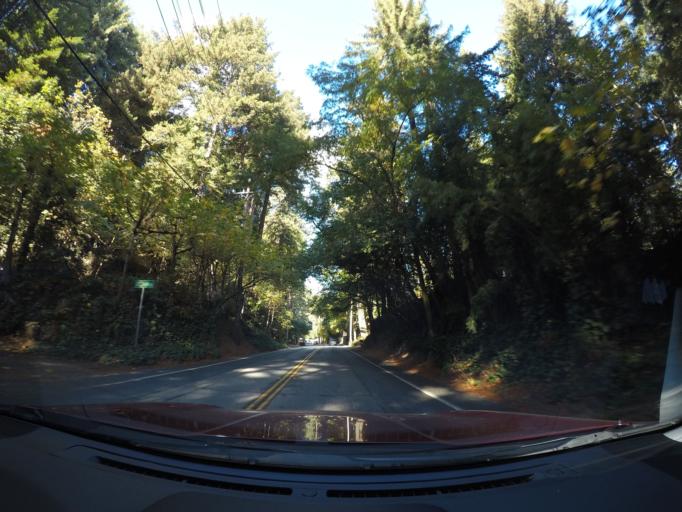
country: US
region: California
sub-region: Santa Cruz County
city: Ben Lomond
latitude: 37.0908
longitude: -122.0947
